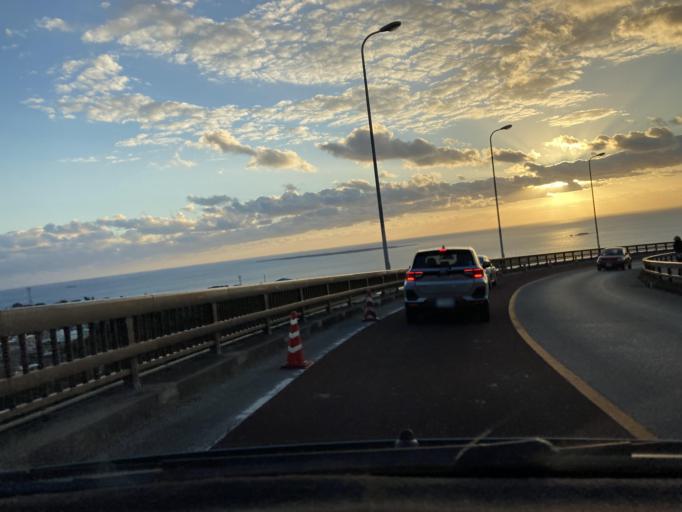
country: JP
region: Okinawa
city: Ginowan
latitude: 26.1674
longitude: 127.8153
